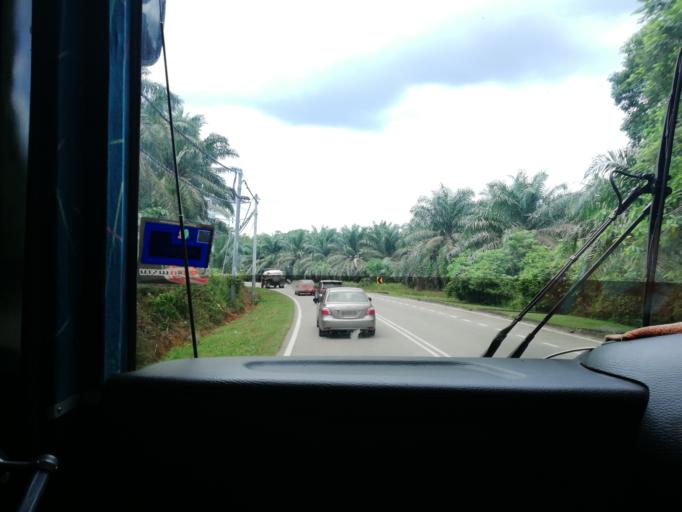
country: MY
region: Perak
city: Parit Buntar
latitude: 5.1934
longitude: 100.6092
